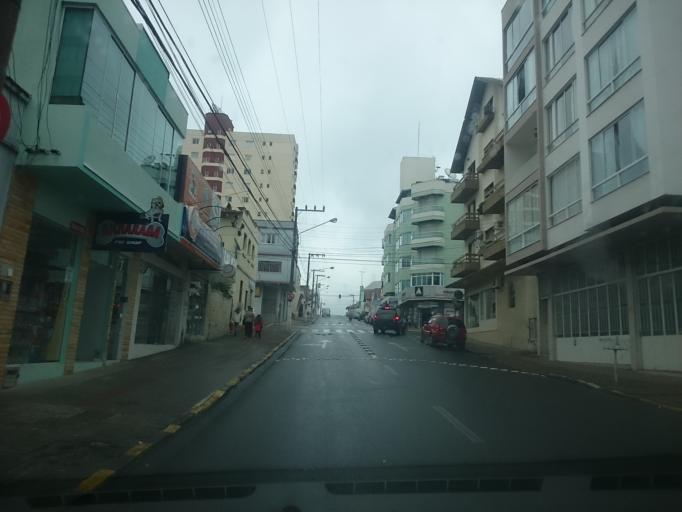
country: BR
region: Santa Catarina
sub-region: Lages
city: Lages
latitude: -27.8182
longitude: -50.3304
